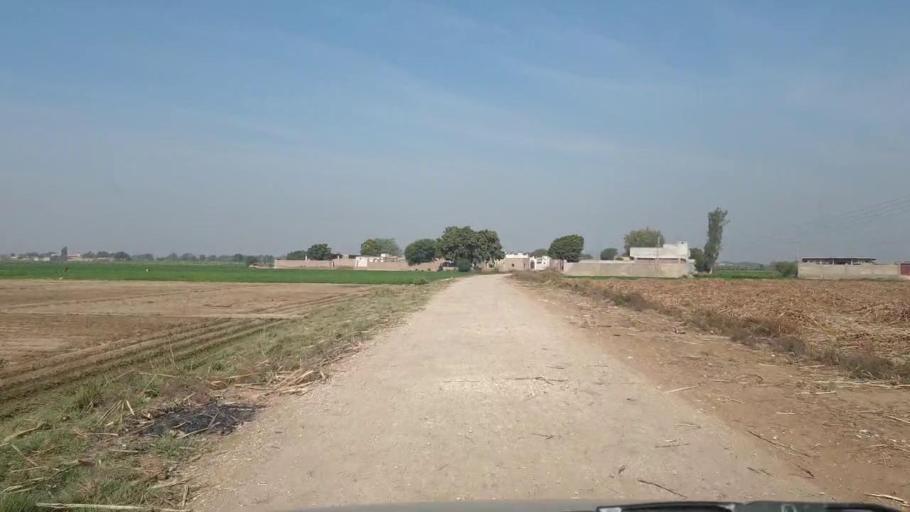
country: PK
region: Sindh
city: Tando Allahyar
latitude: 25.4025
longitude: 68.7446
